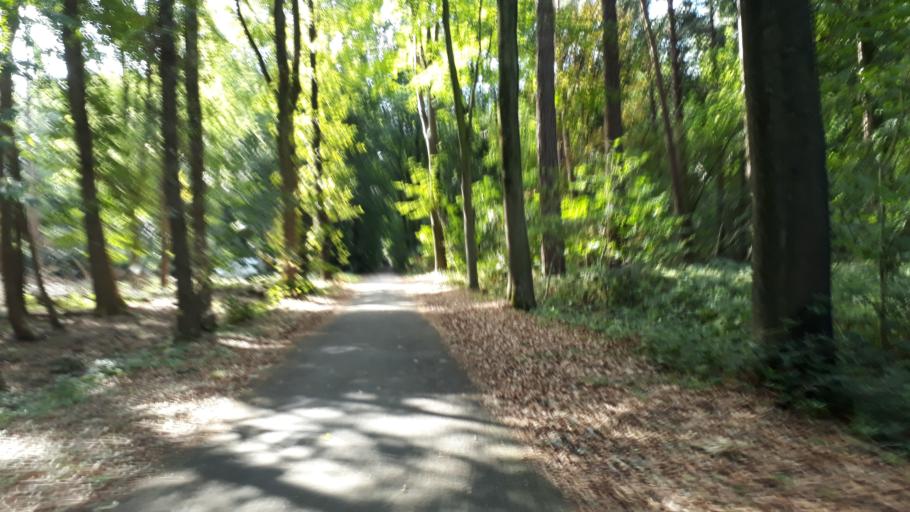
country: BE
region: Flanders
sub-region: Provincie West-Vlaanderen
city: Lichtervelde
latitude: 51.0763
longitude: 3.1450
